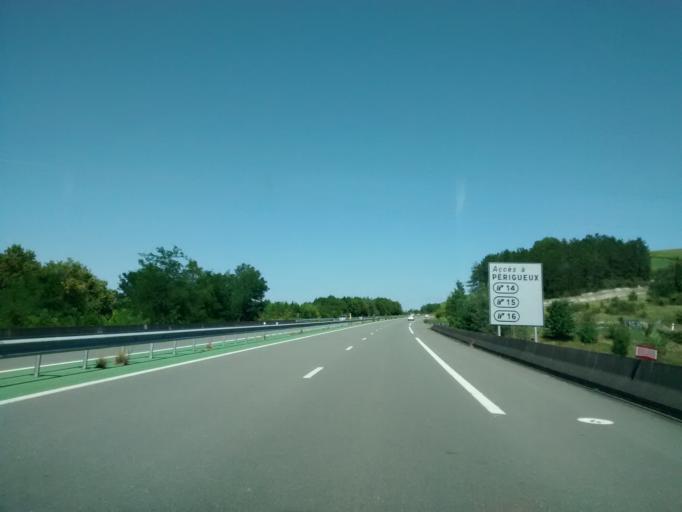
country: FR
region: Aquitaine
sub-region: Departement de la Dordogne
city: Saint-Astier
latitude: 45.1186
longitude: 0.5163
